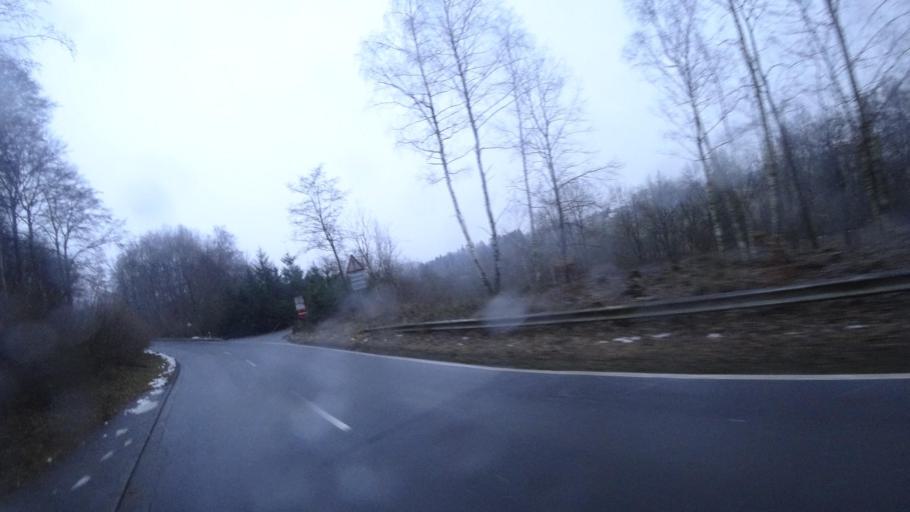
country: DE
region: Rheinland-Pfalz
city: Enspel
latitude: 50.6130
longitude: 7.8875
